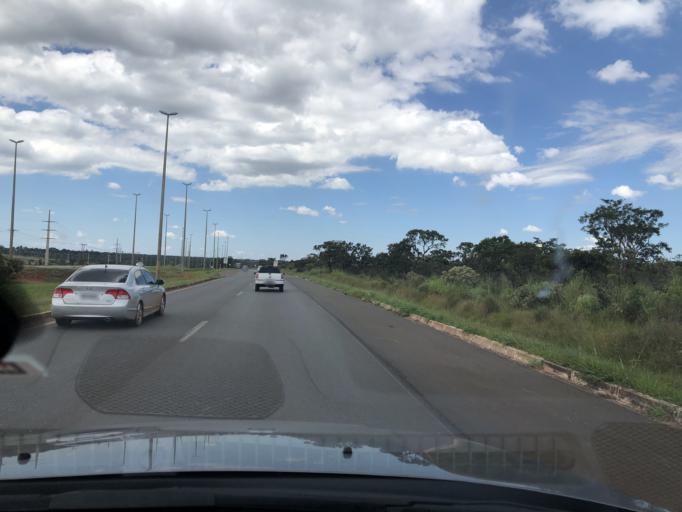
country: BR
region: Federal District
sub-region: Brasilia
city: Brasilia
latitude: -15.9721
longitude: -48.0155
